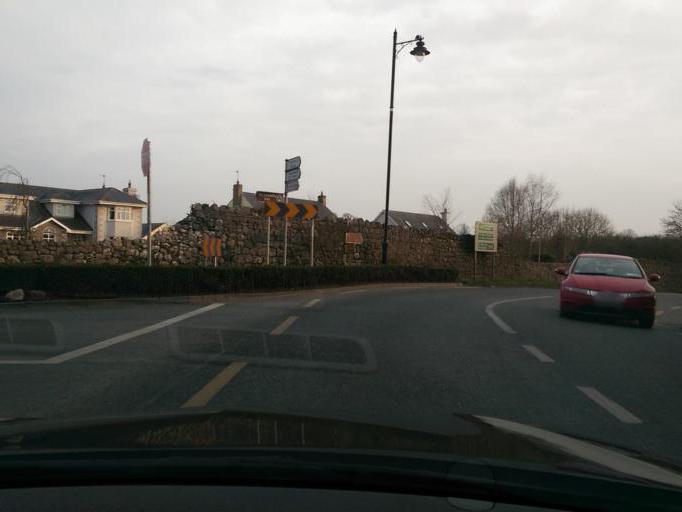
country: IE
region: Leinster
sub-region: An Iarmhi
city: Athlone
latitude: 53.4700
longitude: -7.8638
